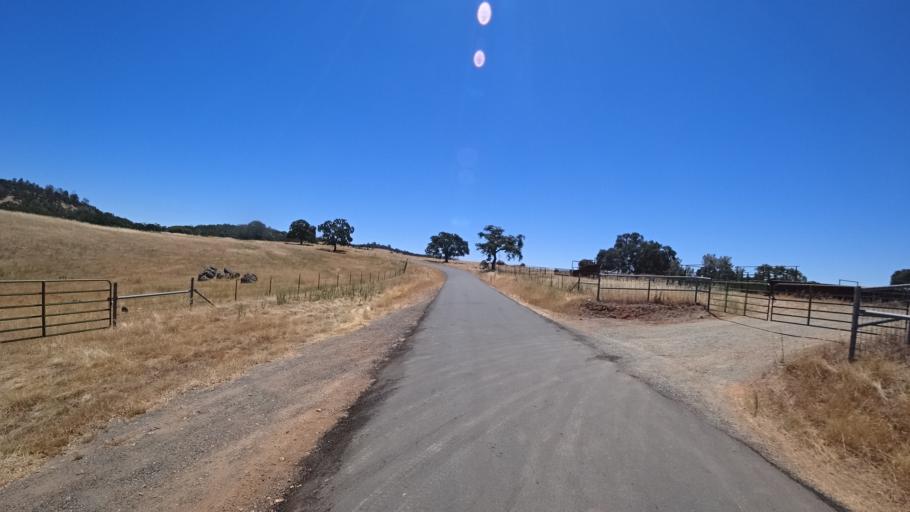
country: US
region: California
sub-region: Calaveras County
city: Rancho Calaveras
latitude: 38.0496
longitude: -120.8000
